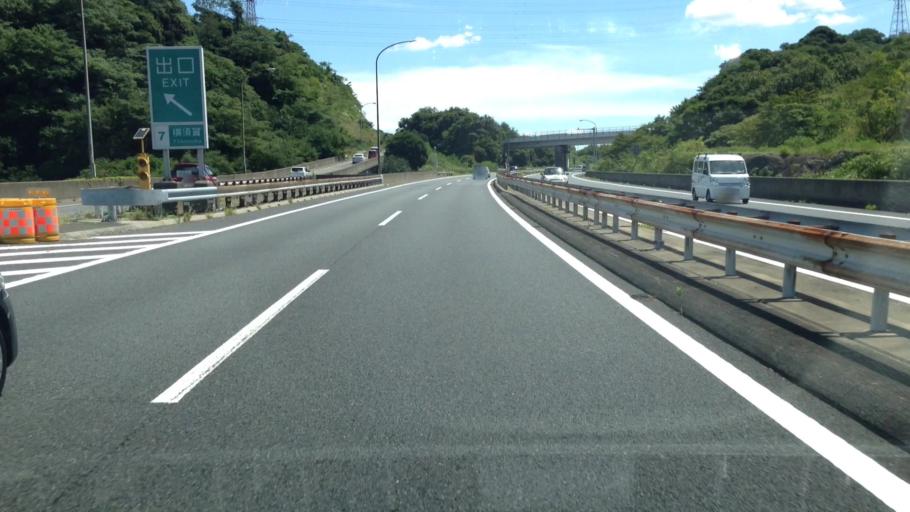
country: JP
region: Kanagawa
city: Yokosuka
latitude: 35.2790
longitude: 139.6324
